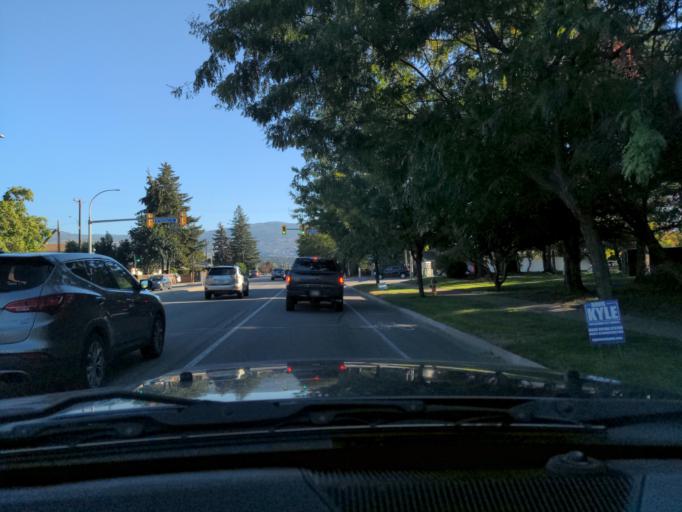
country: CA
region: British Columbia
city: Kelowna
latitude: 49.8580
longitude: -119.4745
